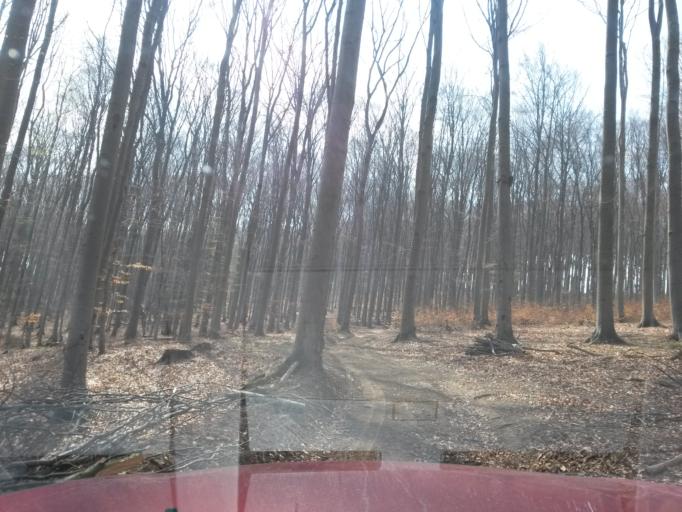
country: SK
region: Presovsky
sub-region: Okres Presov
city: Presov
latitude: 48.9333
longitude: 21.1398
